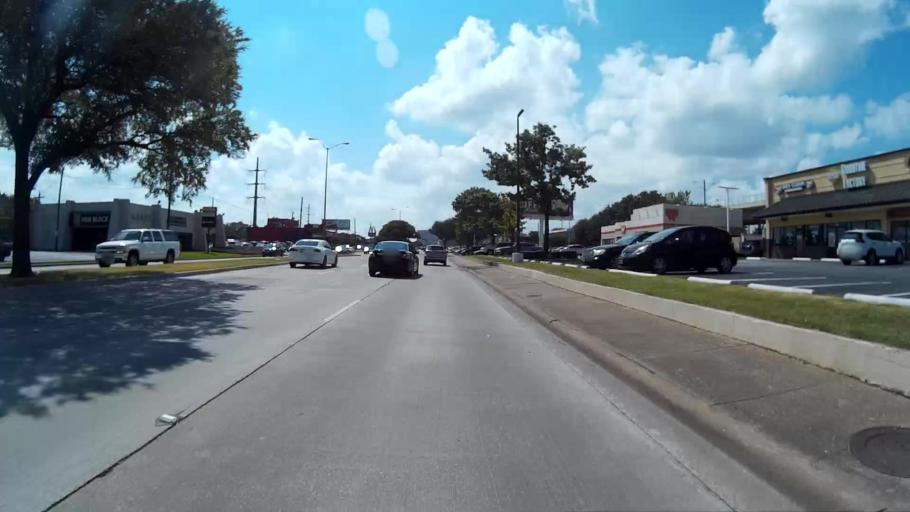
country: US
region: Texas
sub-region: Dallas County
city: University Park
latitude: 32.8599
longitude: -96.7681
